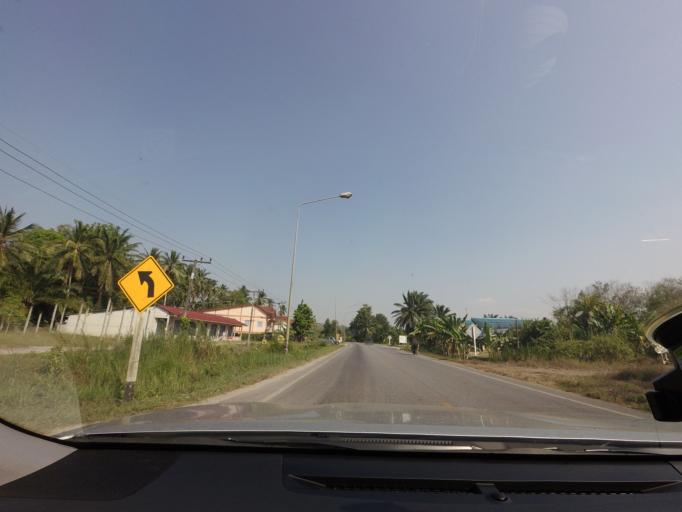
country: TH
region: Surat Thani
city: Chai Buri
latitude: 8.6020
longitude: 99.0157
